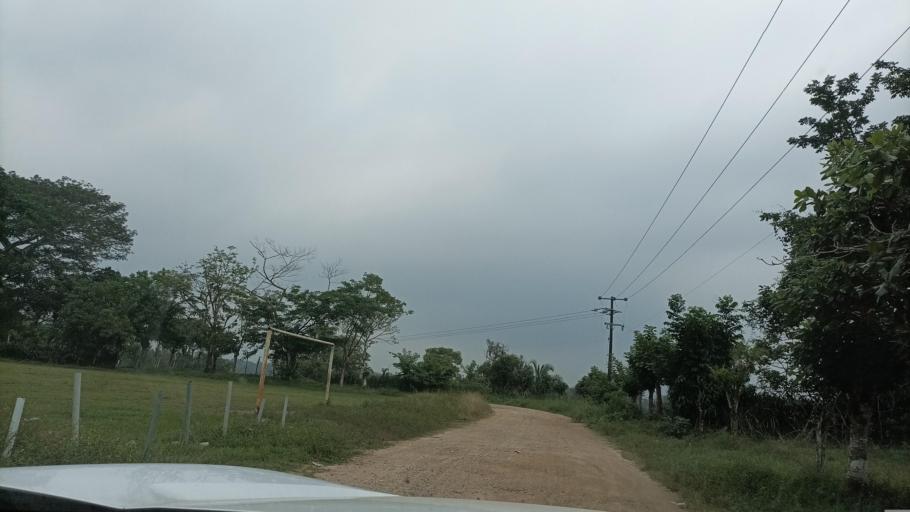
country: MX
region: Veracruz
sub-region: Uxpanapa
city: Poblado 10
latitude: 17.5422
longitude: -94.2370
